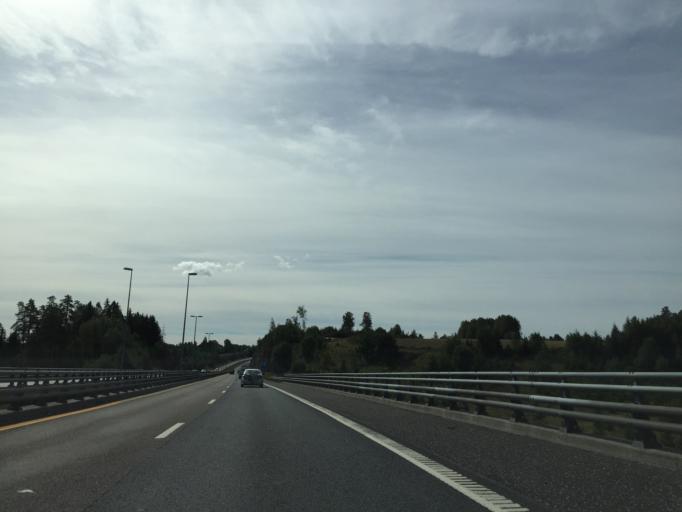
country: NO
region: Akershus
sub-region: As
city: As
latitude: 59.6766
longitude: 10.7417
